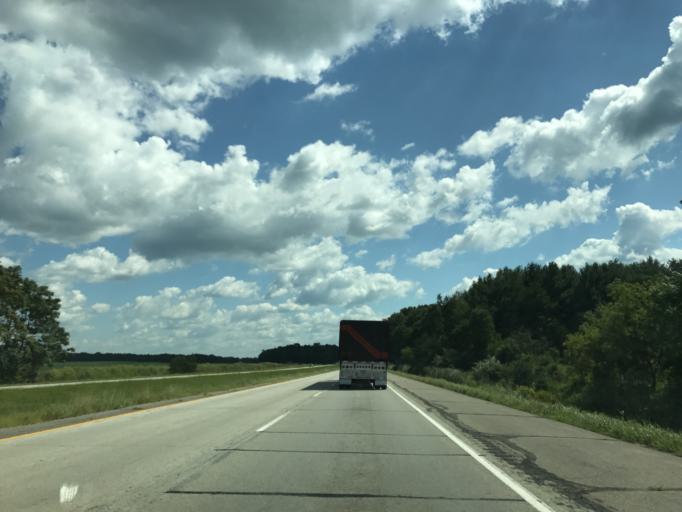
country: US
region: Indiana
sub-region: Starke County
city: Koontz Lake
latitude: 41.3644
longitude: -86.4260
